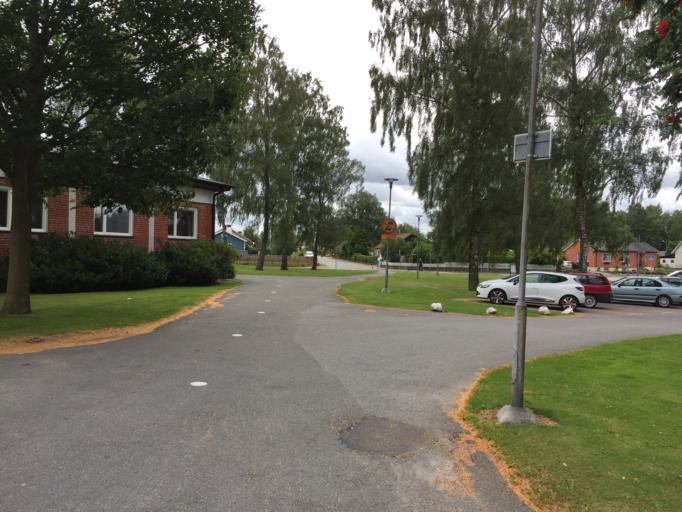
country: SE
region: Skane
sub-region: Hassleholms Kommun
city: Sosdala
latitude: 56.0419
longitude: 13.6766
